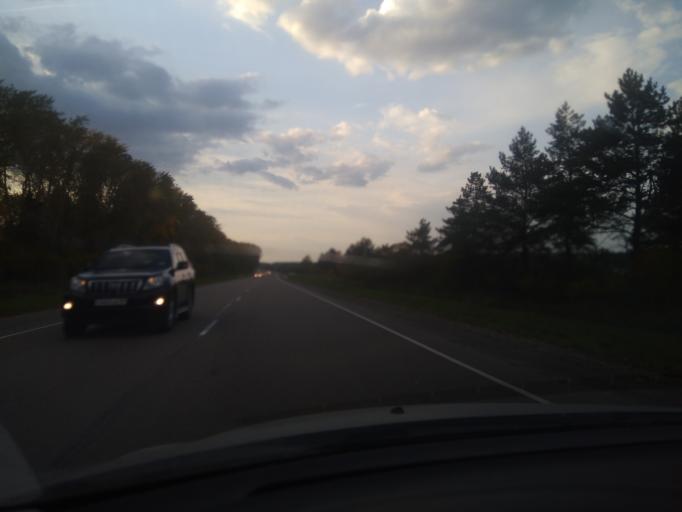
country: RU
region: Sverdlovsk
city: Dvurechensk
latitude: 56.6706
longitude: 61.1478
